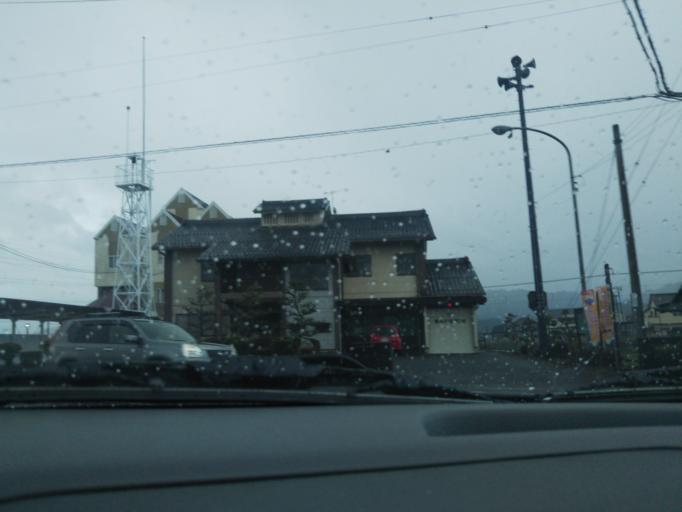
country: JP
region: Shiga Prefecture
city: Minakuchicho-matoba
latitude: 34.9495
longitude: 136.1585
